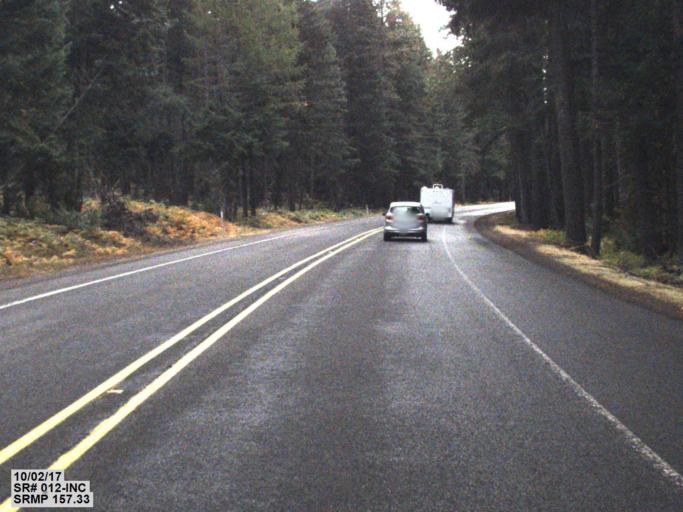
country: US
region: Washington
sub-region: Yakima County
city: Tieton
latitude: 46.6509
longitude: -121.2812
